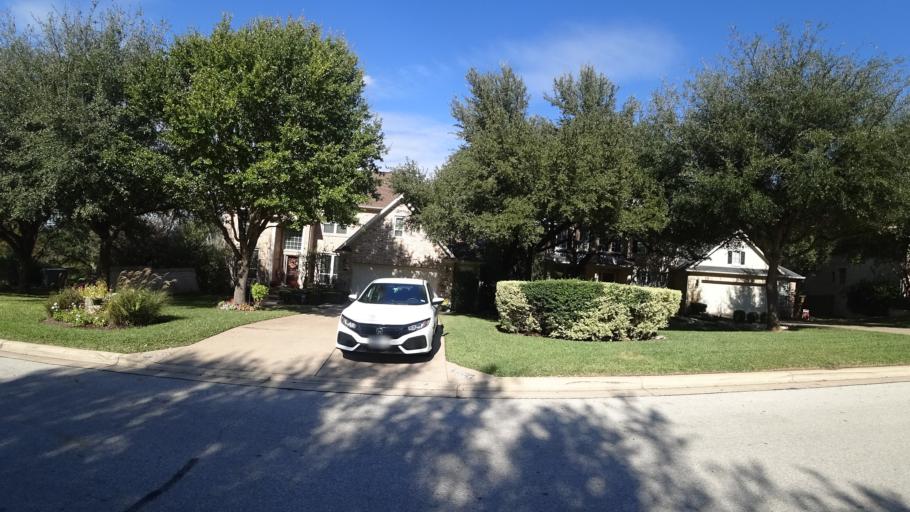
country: US
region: Texas
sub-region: Travis County
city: Hudson Bend
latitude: 30.3796
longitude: -97.9050
